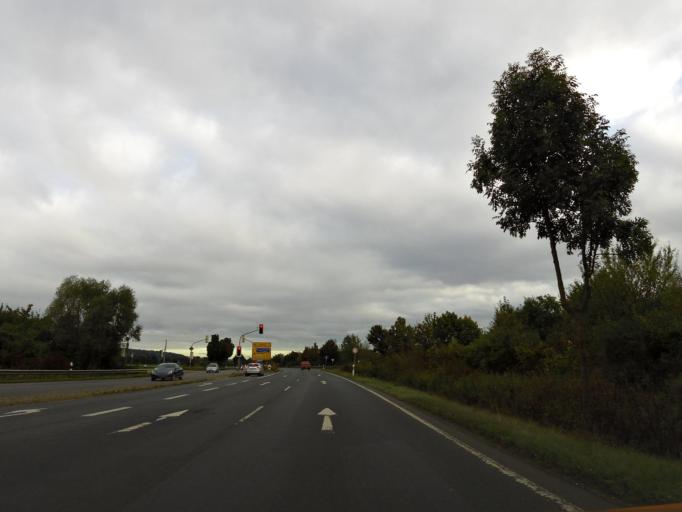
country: DE
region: Lower Saxony
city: Goettingen
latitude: 51.5574
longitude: 9.9205
